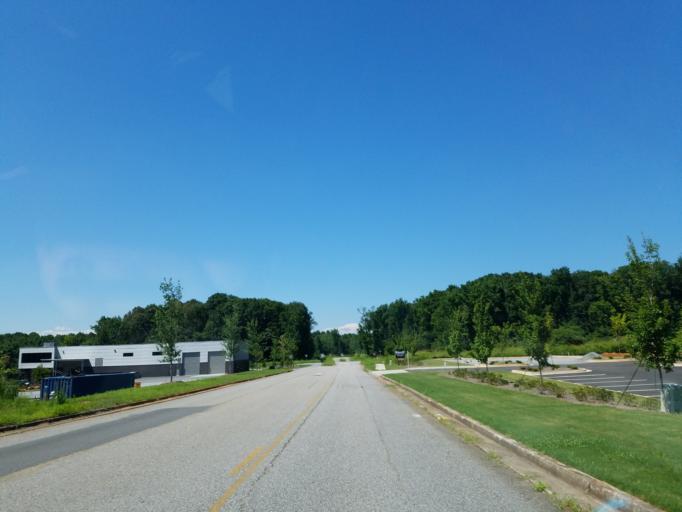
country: US
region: Georgia
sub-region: Forsyth County
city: Cumming
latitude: 34.2762
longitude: -84.0754
